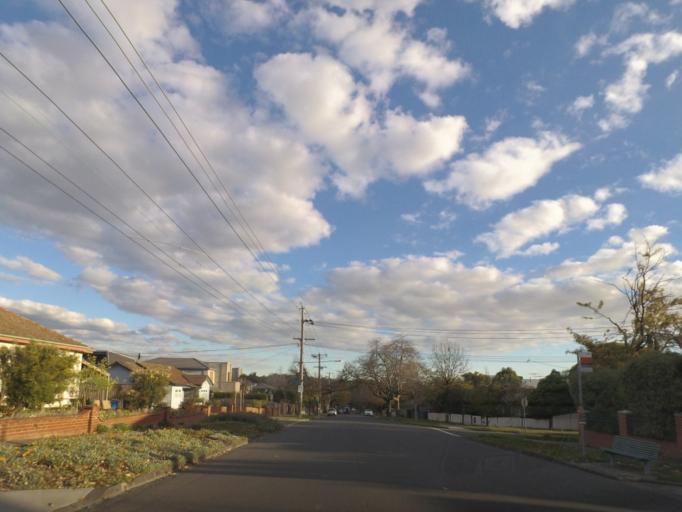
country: AU
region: Victoria
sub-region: Whitehorse
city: Surrey Hills
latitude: -37.8393
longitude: 145.0928
